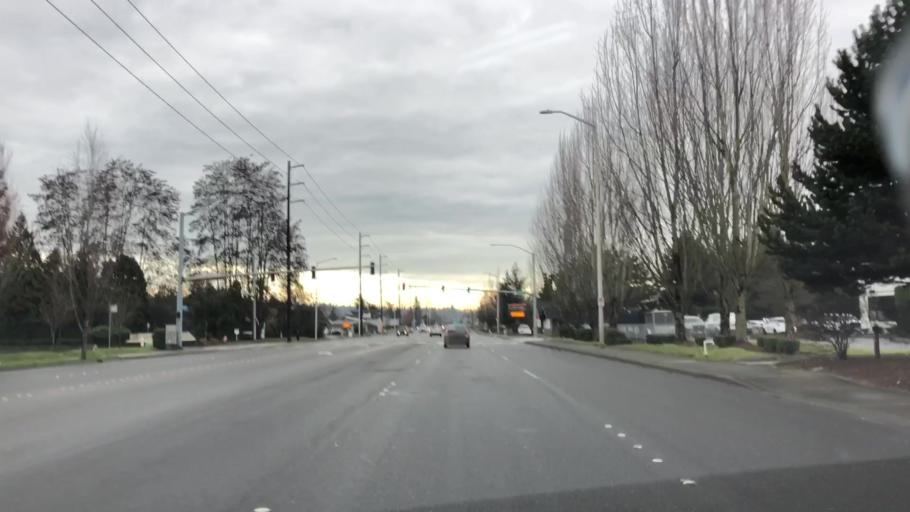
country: US
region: Washington
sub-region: King County
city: Kent
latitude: 47.4093
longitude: -122.2281
